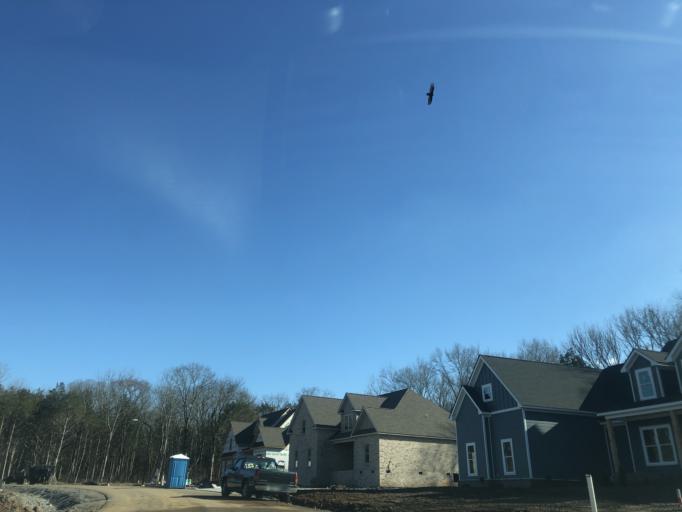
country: US
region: Tennessee
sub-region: Rutherford County
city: Smyrna
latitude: 35.9504
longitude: -86.4181
